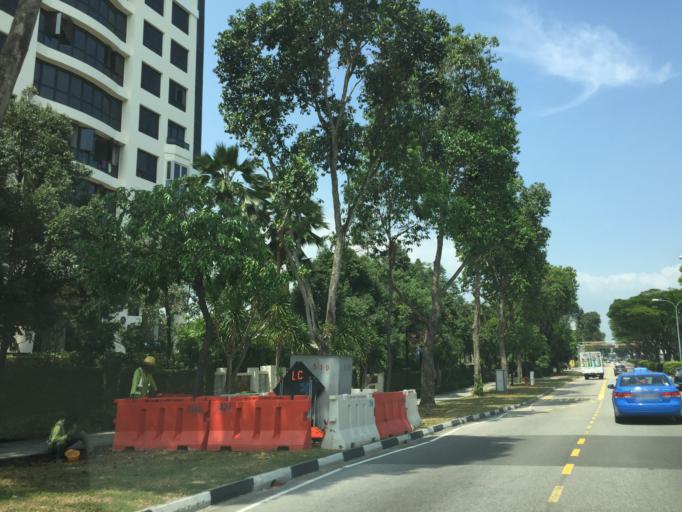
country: SG
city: Singapore
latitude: 1.3385
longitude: 103.9496
